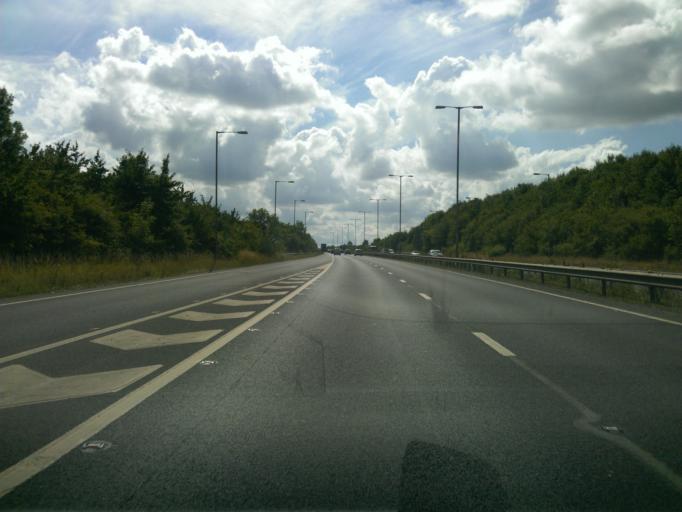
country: GB
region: England
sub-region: Northamptonshire
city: Rothwell
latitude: 52.4151
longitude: -0.8177
